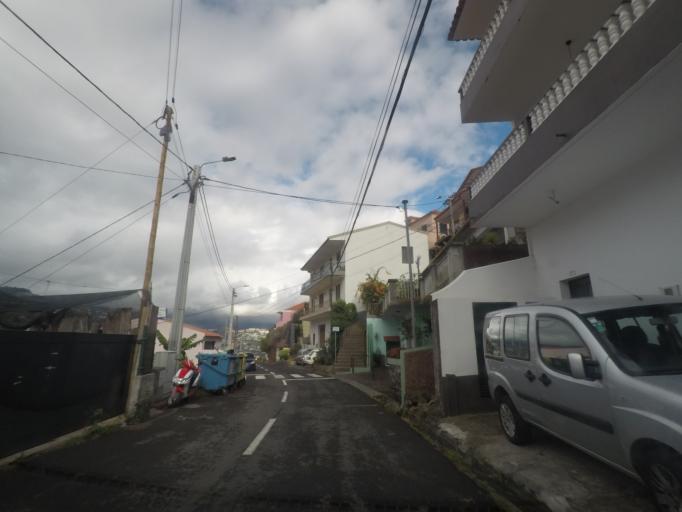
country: PT
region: Madeira
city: Camara de Lobos
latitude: 32.6556
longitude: -16.9939
